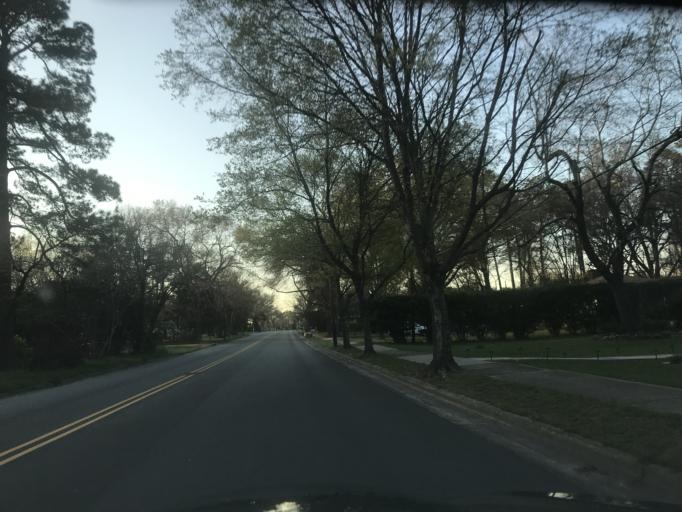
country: US
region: North Carolina
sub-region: Wake County
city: Raleigh
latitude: 35.7769
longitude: -78.6059
